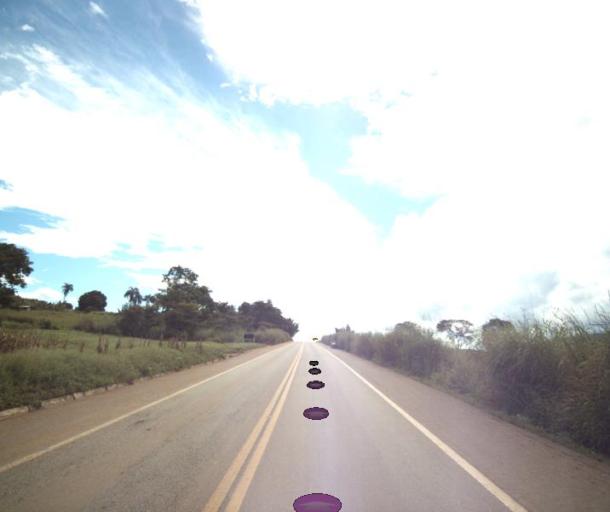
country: BR
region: Goias
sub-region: Pirenopolis
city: Pirenopolis
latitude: -16.0124
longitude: -49.1205
